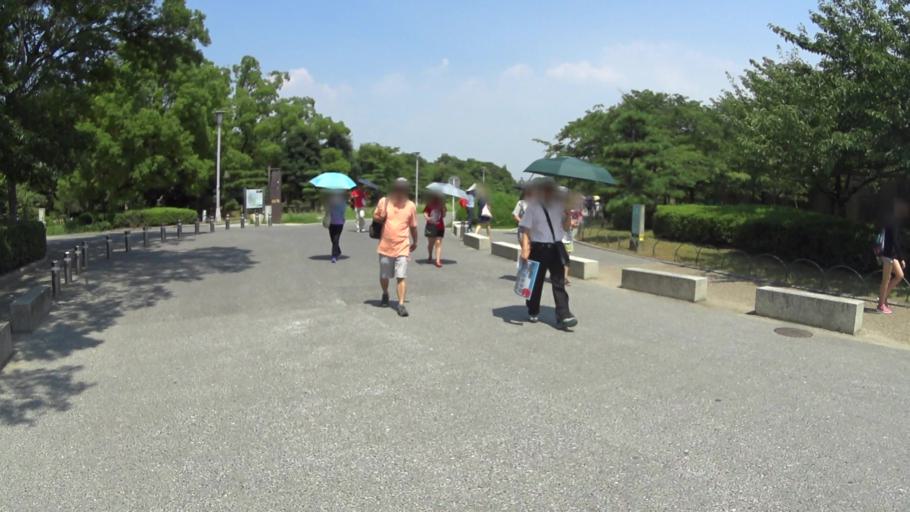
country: JP
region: Osaka
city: Osaka-shi
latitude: 34.6852
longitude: 135.5274
